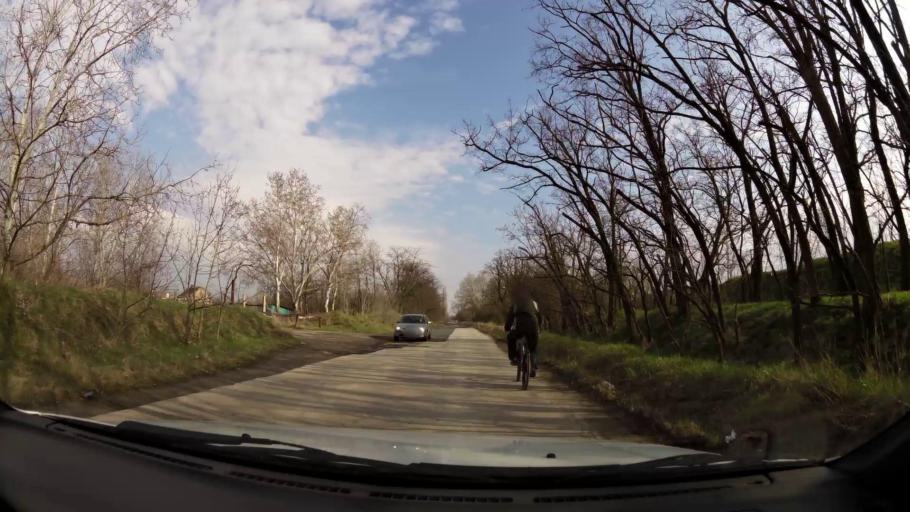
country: HU
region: Budapest
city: Budapest XVII. keruelet
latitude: 47.5062
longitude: 19.2569
